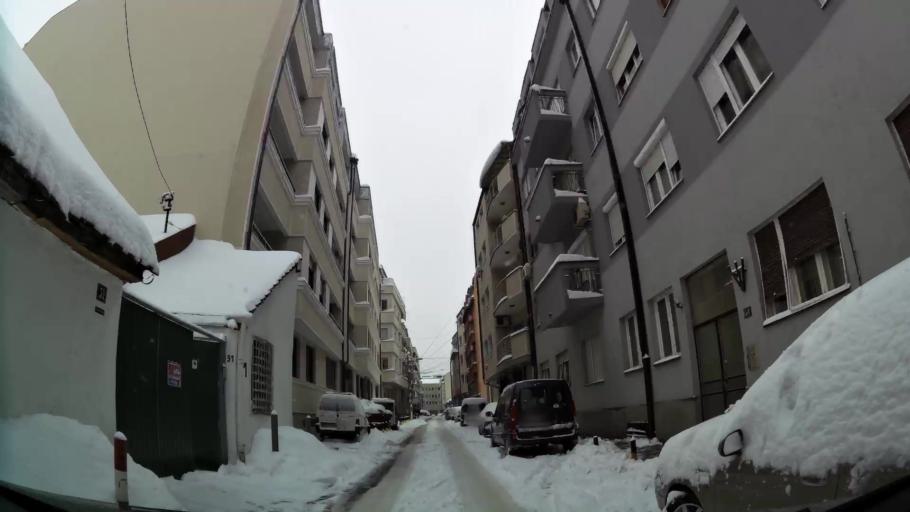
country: RS
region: Central Serbia
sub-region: Belgrade
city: Vracar
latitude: 44.7966
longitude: 20.4723
